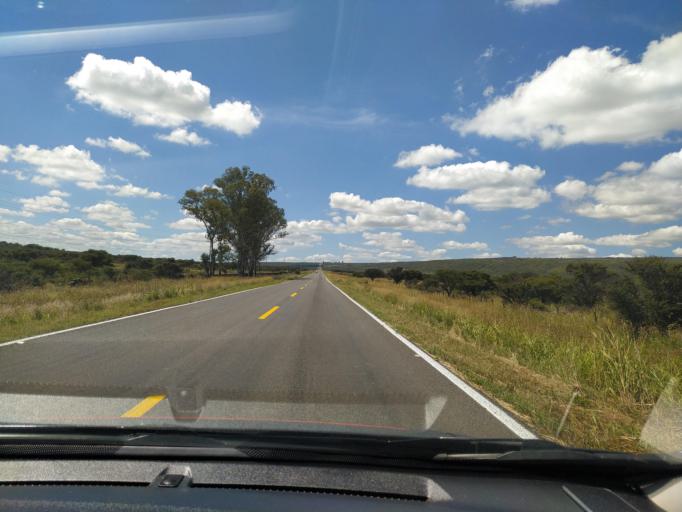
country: MX
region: Jalisco
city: San Miguel el Alto
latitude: 21.0163
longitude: -102.4790
